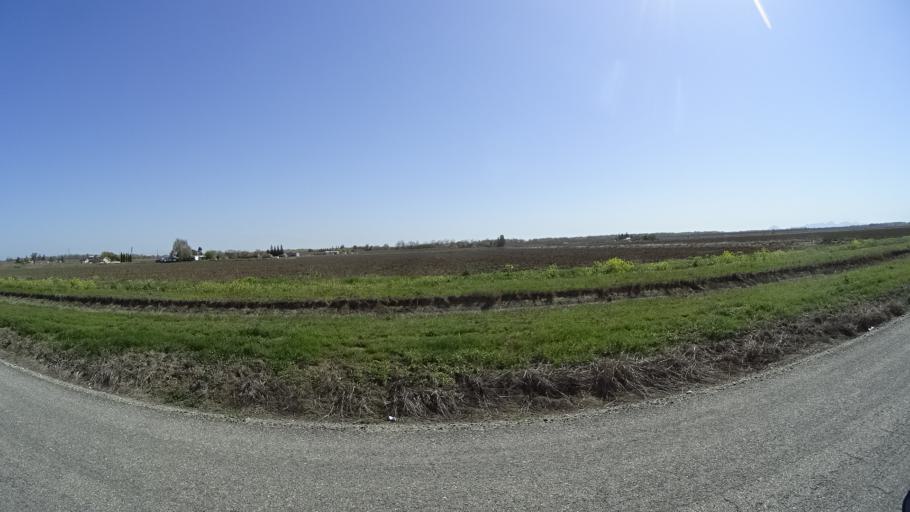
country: US
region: California
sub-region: Glenn County
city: Willows
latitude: 39.4335
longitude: -122.0324
